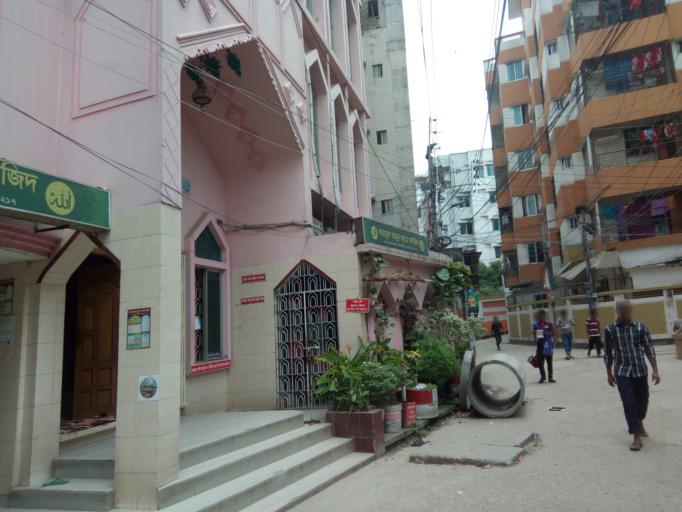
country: BD
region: Dhaka
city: Paltan
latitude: 23.7490
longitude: 90.4108
